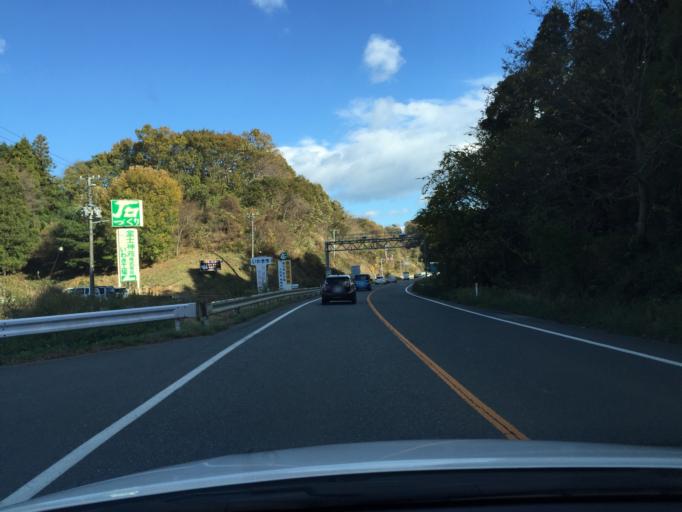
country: JP
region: Fukushima
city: Iwaki
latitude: 37.1820
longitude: 140.9926
